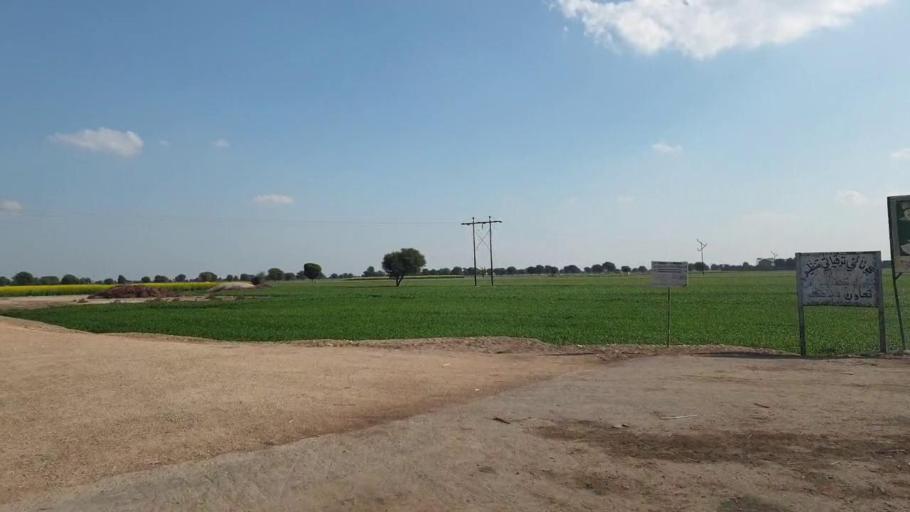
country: PK
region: Sindh
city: Shahpur Chakar
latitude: 26.1022
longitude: 68.5689
